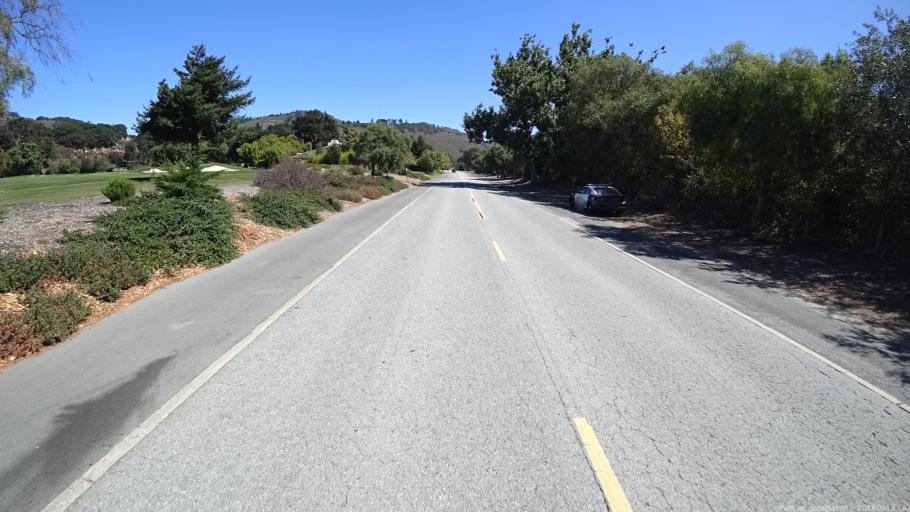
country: US
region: California
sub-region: Monterey County
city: Del Rey Oaks
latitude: 36.5310
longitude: -121.8536
